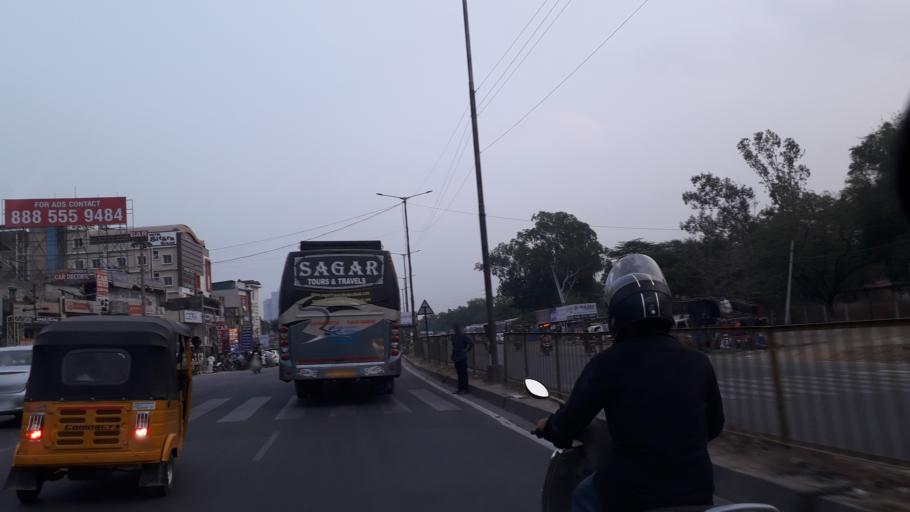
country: IN
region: Telangana
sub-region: Medak
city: Serilingampalle
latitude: 17.5023
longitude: 78.3118
